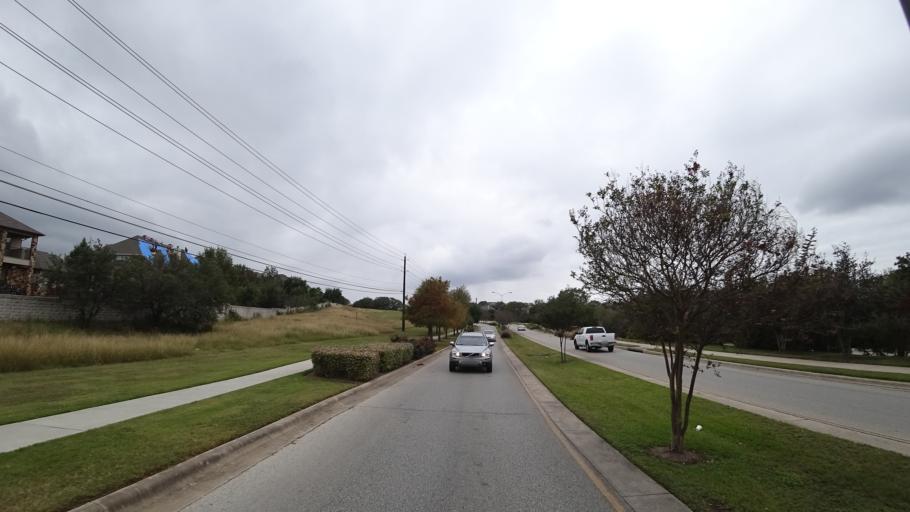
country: US
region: Texas
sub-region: Travis County
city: Hudson Bend
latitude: 30.3607
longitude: -97.9020
